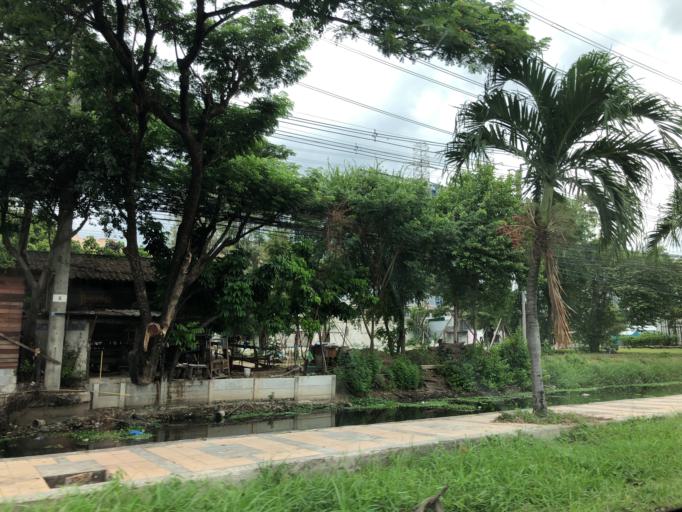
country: TH
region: Bangkok
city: Lak Si
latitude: 13.8932
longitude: 100.5538
